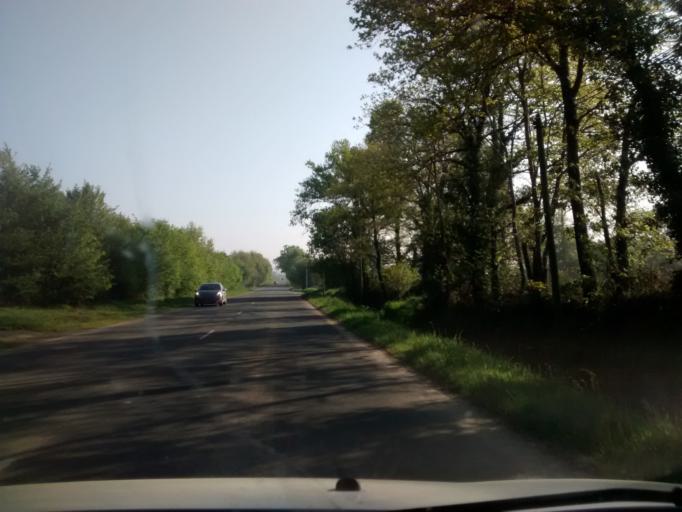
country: FR
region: Brittany
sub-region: Departement d'Ille-et-Vilaine
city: Saint-Jean-sur-Couesnon
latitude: 48.2803
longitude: -1.3830
